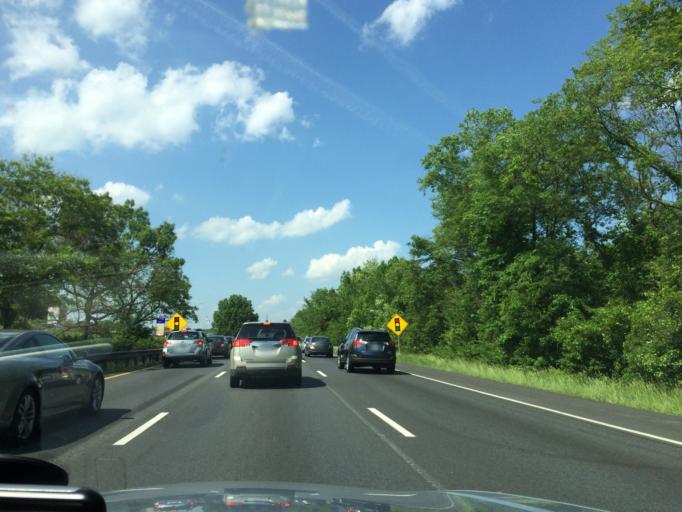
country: US
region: Maryland
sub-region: Anne Arundel County
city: Crofton
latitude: 39.0065
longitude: -76.6987
